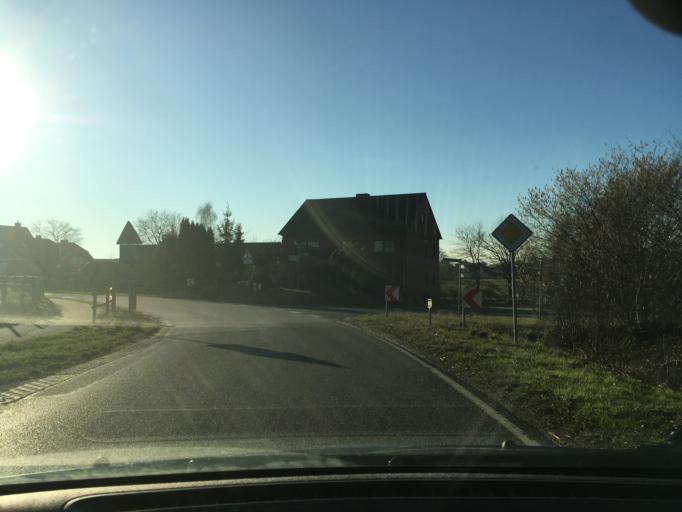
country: DE
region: Schleswig-Holstein
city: Schulendorf
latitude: 53.4735
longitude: 10.5703
